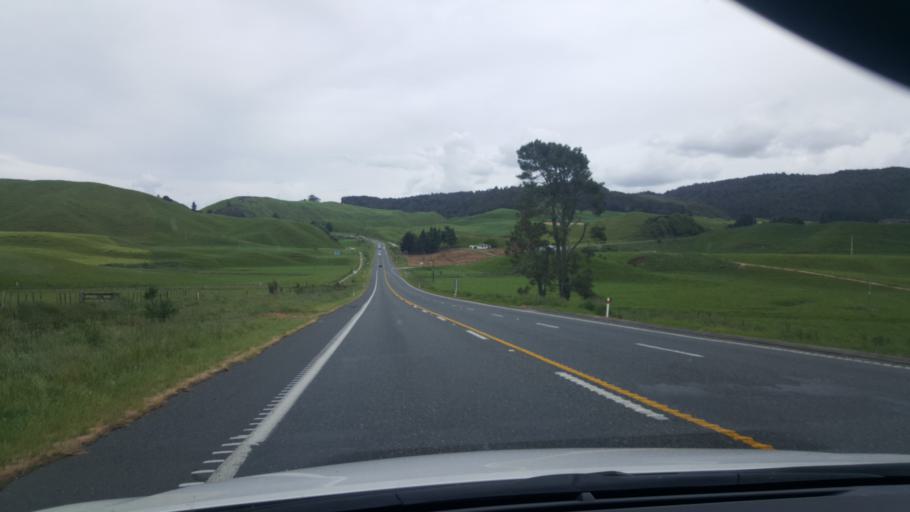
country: NZ
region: Bay of Plenty
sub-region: Rotorua District
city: Rotorua
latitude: -38.2529
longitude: 176.3185
